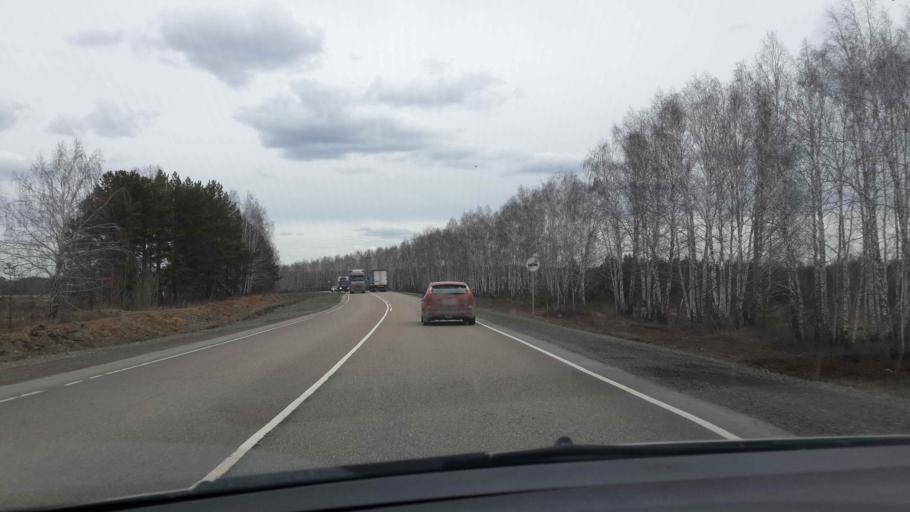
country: RU
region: Sverdlovsk
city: Zarechnyy
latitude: 56.7414
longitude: 61.2664
